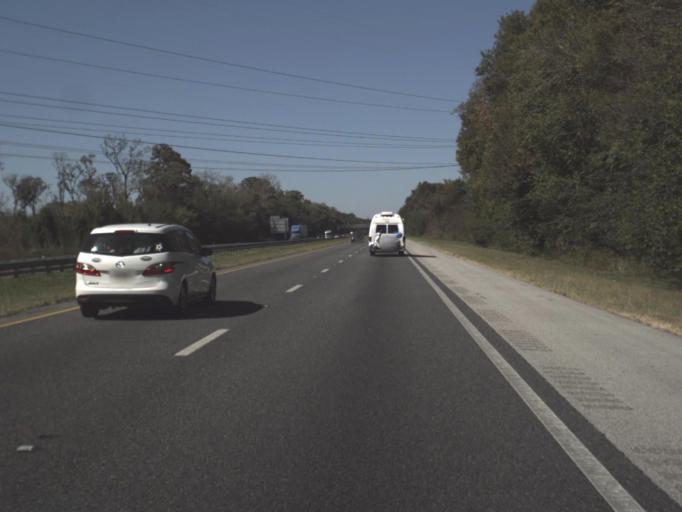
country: US
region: Florida
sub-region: Sumter County
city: Wildwood
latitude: 28.8432
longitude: -82.0629
